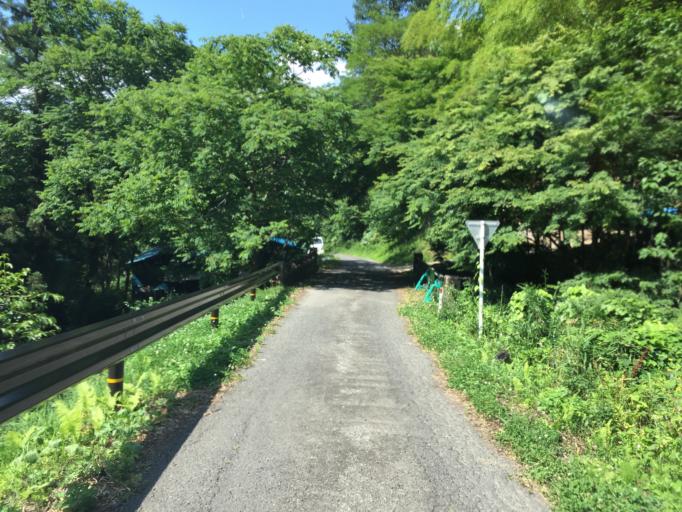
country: JP
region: Fukushima
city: Yanagawamachi-saiwaicho
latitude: 37.7815
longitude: 140.6583
